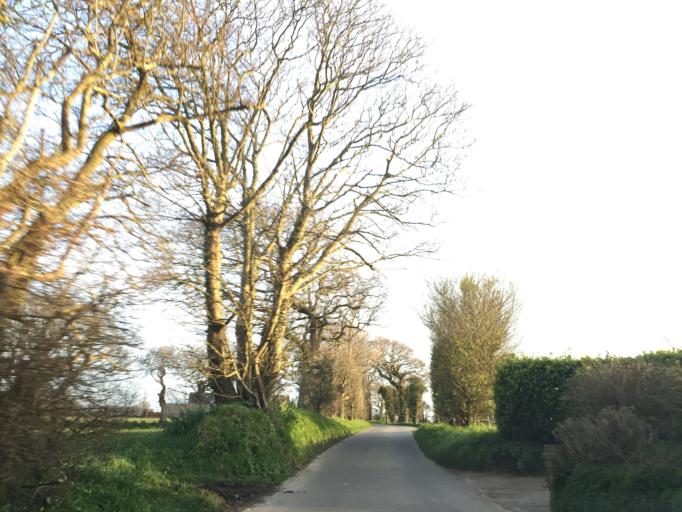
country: JE
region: St Helier
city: Saint Helier
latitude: 49.2296
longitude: -2.0550
